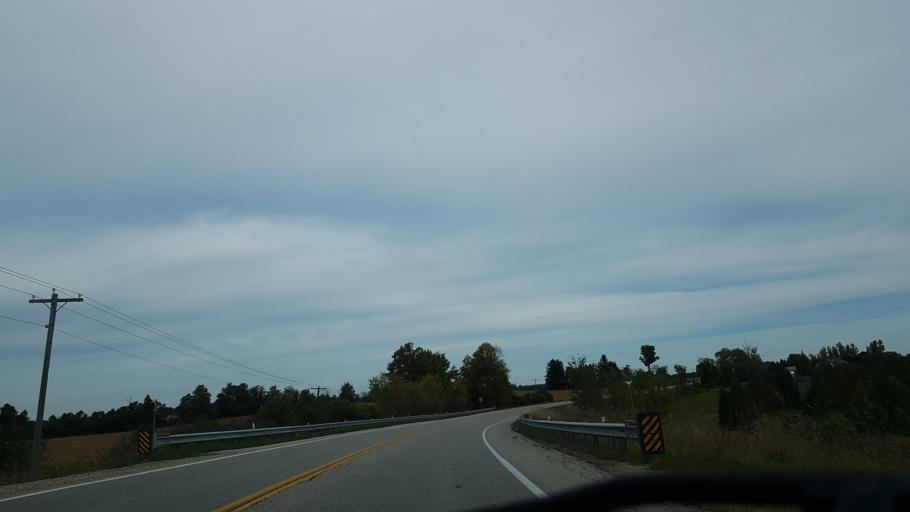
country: CA
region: Ontario
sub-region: Wellington County
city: Guelph
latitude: 43.6258
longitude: -80.2133
